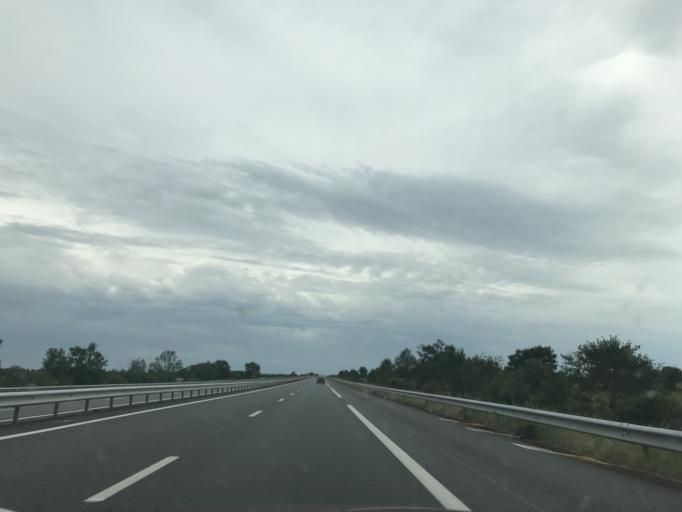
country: FR
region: Centre
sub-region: Departement du Cher
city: Saint-Amand-Montrond
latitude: 46.6244
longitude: 2.5034
